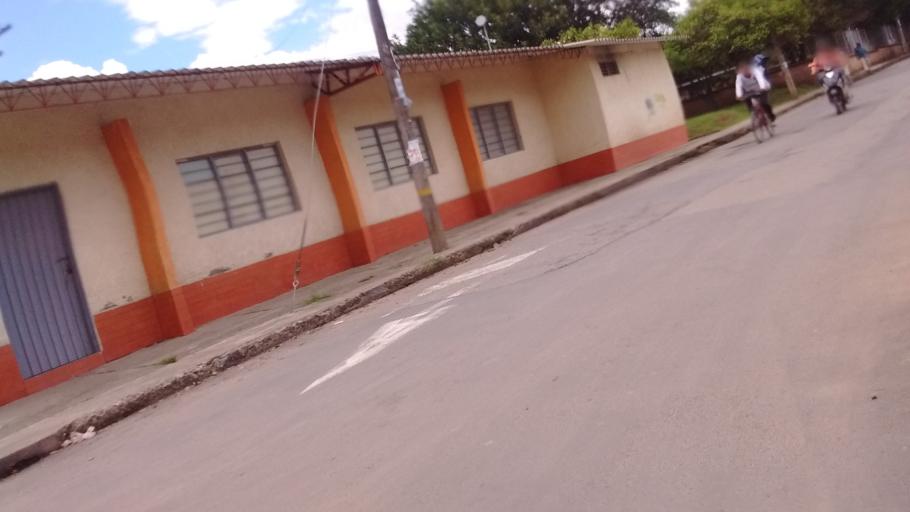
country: CO
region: Cauca
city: Popayan
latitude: 2.4572
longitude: -76.5883
